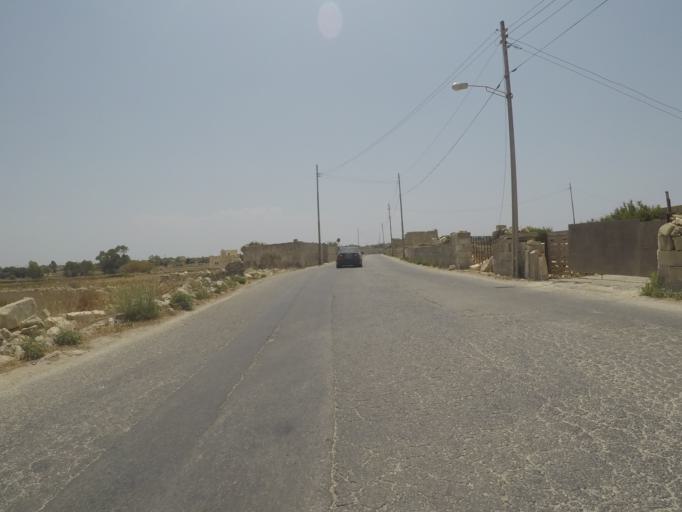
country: MT
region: Is-Siggiewi
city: Siggiewi
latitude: 35.8487
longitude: 14.4338
